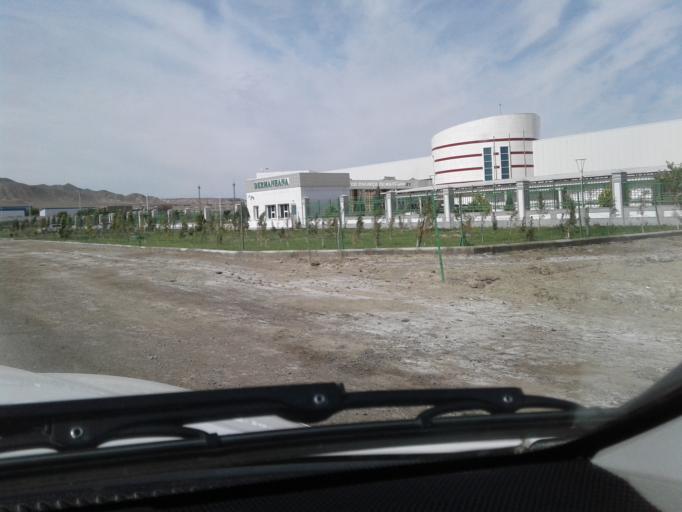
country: TM
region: Balkan
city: Gazanjyk
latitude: 39.2510
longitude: 55.4881
